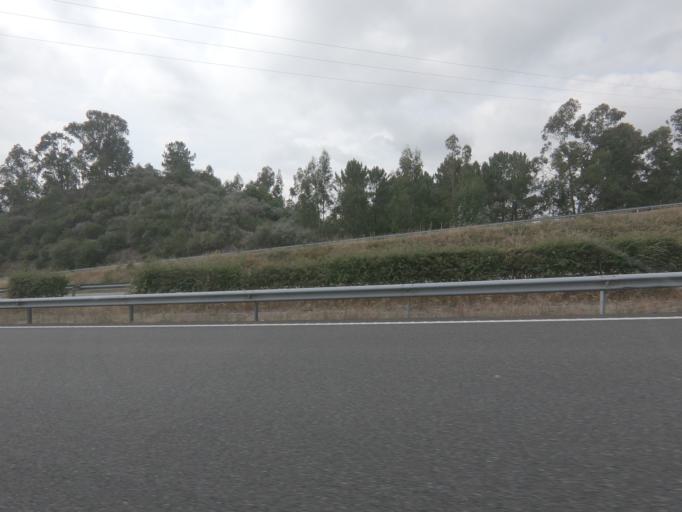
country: ES
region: Galicia
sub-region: Provincia de Pontevedra
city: Ponteareas
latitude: 42.1490
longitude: -8.4295
